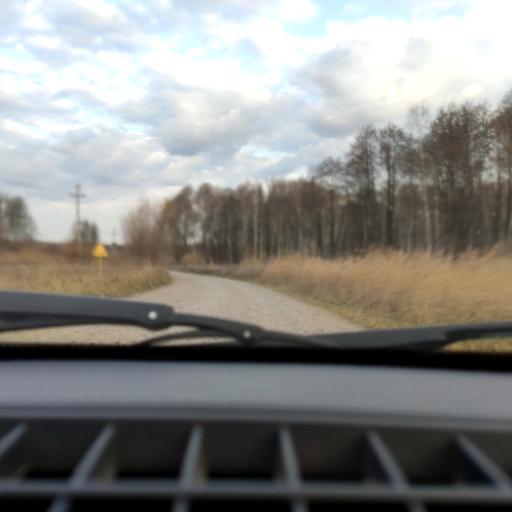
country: RU
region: Bashkortostan
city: Avdon
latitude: 54.6330
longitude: 55.7318
